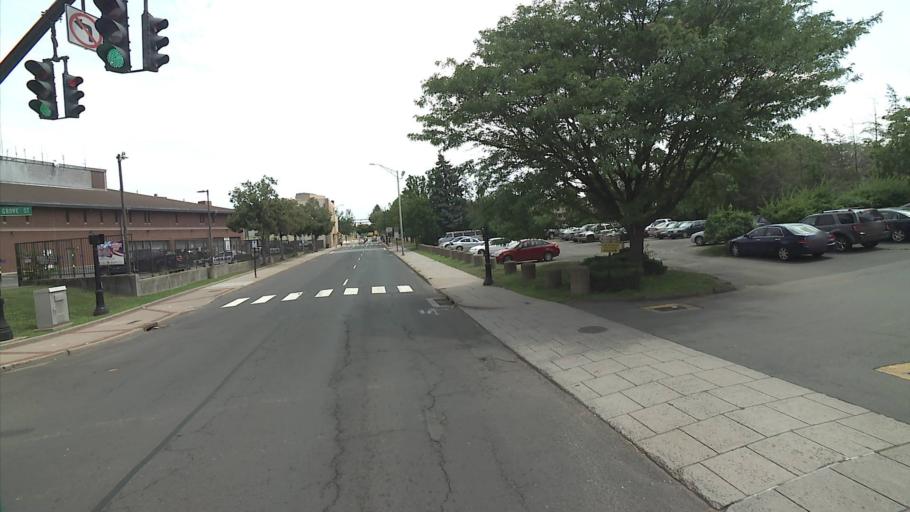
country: US
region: Connecticut
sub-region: New Haven County
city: Meriden
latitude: 41.5369
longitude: -72.8049
